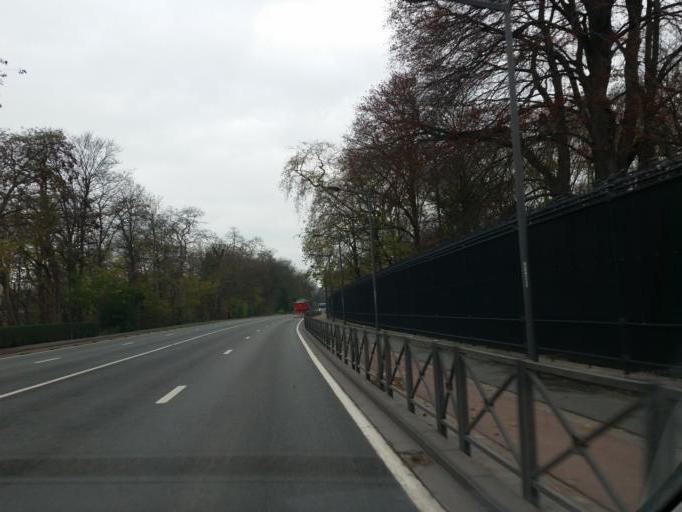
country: BE
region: Brussels Capital
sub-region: Bruxelles-Capitale
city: Brussels
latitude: 50.8824
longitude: 4.3547
